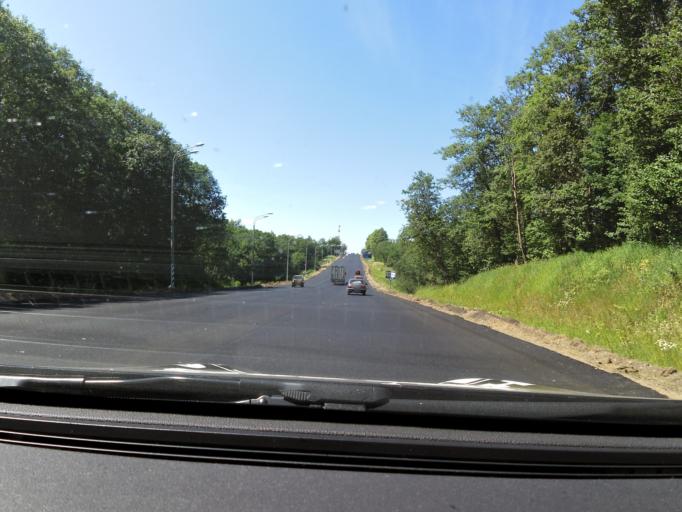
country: RU
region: Novgorod
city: Valday
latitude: 57.9509
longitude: 33.3020
